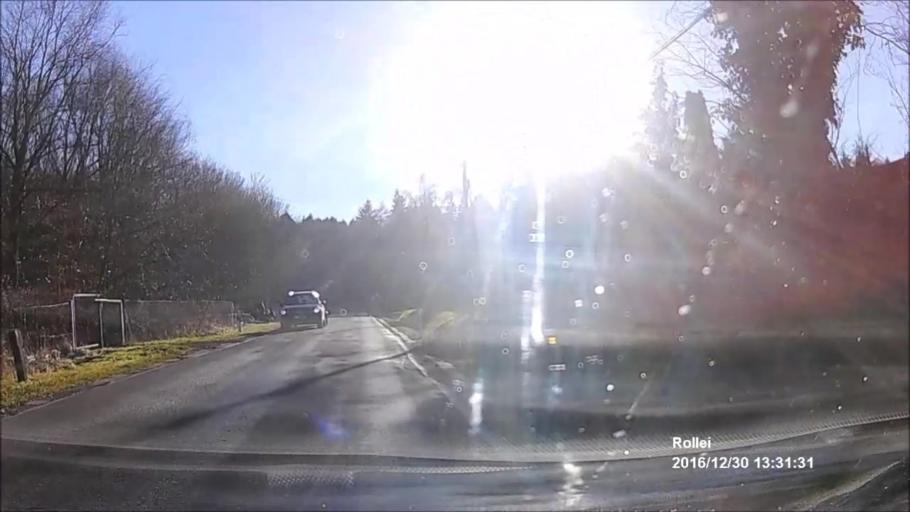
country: DE
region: Thuringia
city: Klettbach
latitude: 50.9347
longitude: 11.1032
